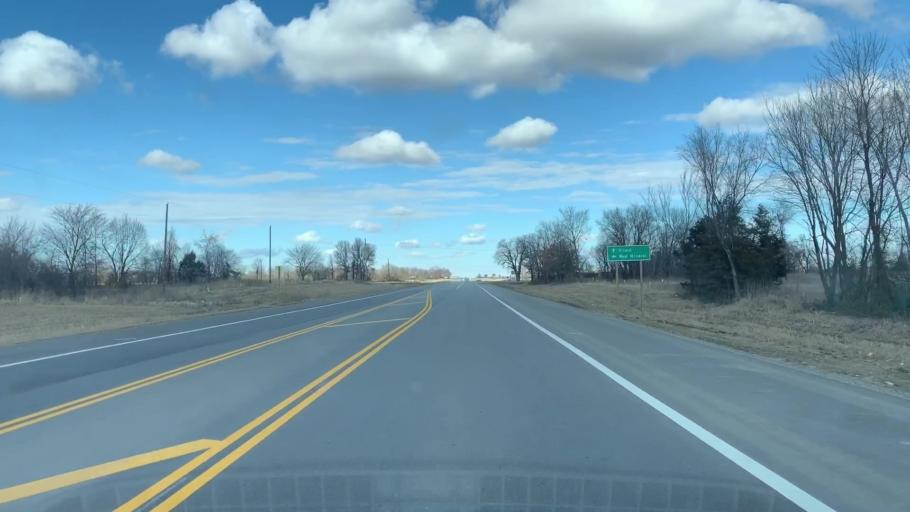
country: US
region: Kansas
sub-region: Cherokee County
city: Columbus
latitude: 37.2785
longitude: -94.8321
